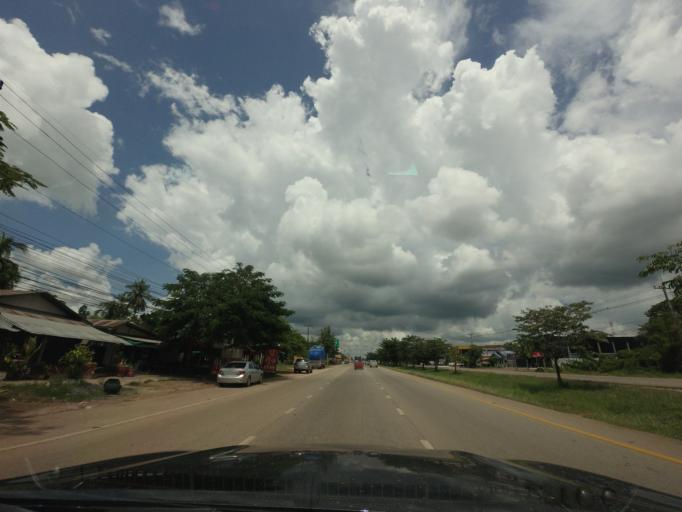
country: TH
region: Changwat Udon Thani
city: Udon Thani
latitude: 17.5280
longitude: 102.7995
